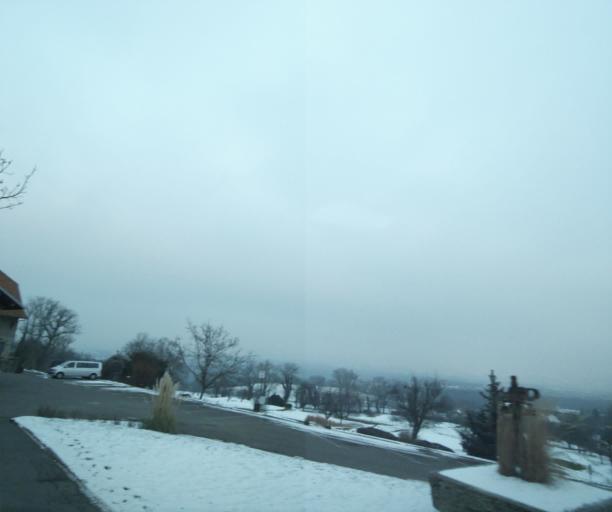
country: FR
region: Rhone-Alpes
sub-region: Departement de la Haute-Savoie
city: Reignier-Esery
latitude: 46.1431
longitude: 6.2417
